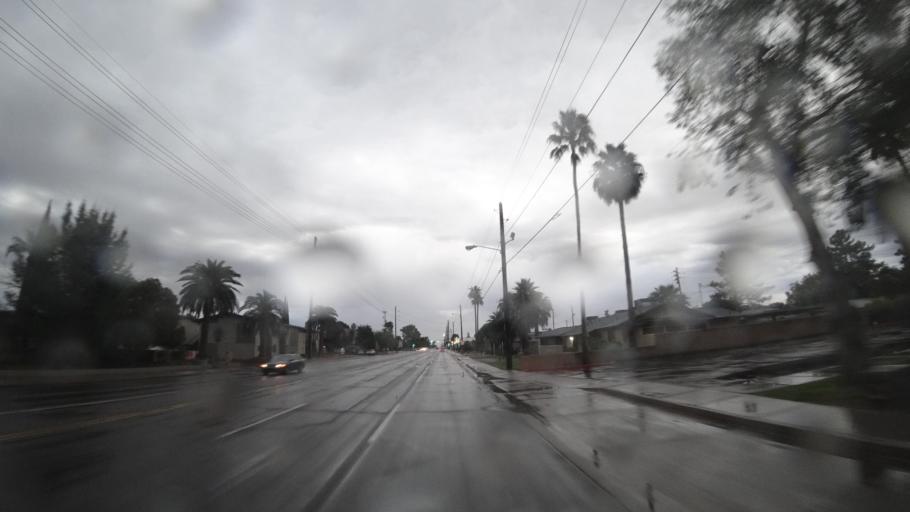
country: US
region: Arizona
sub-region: Maricopa County
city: Paradise Valley
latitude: 33.4800
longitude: -111.9721
